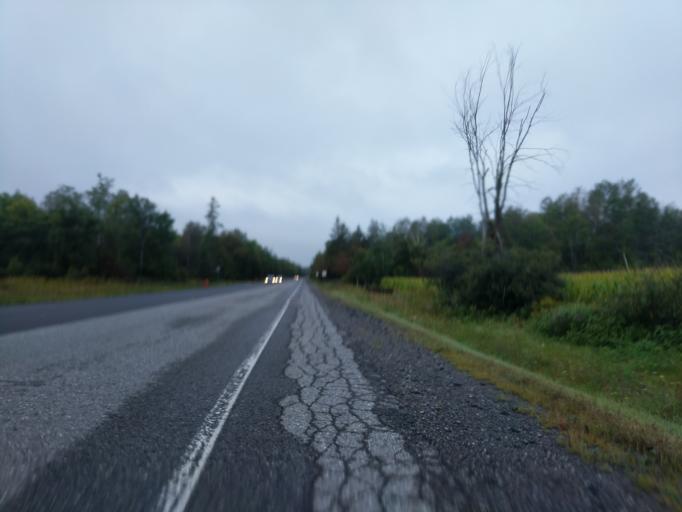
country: CA
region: Ontario
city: Bells Corners
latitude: 45.3214
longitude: -75.8514
